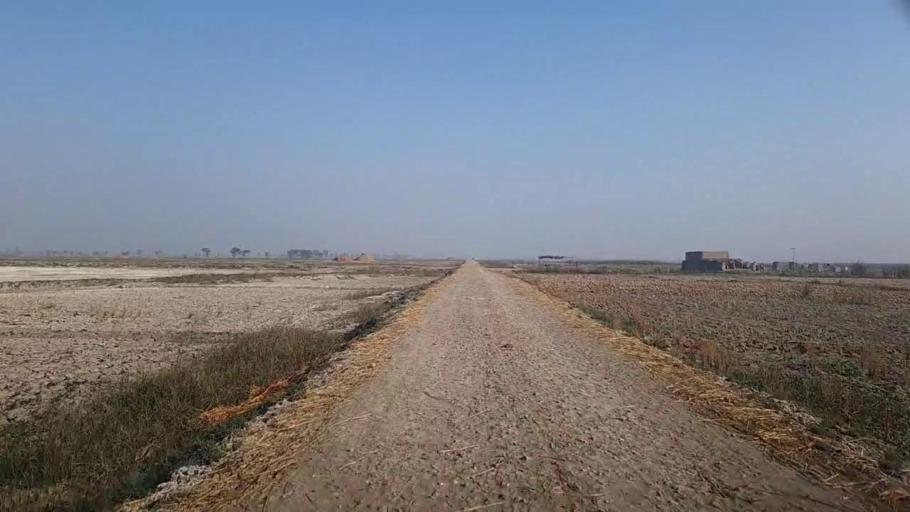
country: PK
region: Sindh
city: Radhan
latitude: 27.1340
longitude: 67.9043
